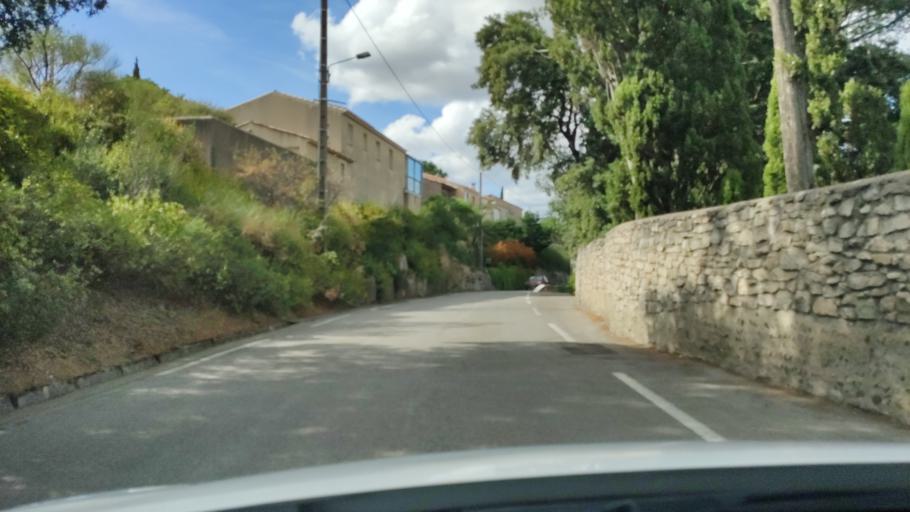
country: FR
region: Languedoc-Roussillon
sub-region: Departement du Gard
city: Villeneuve-les-Avignon
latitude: 43.9608
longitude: 4.7896
